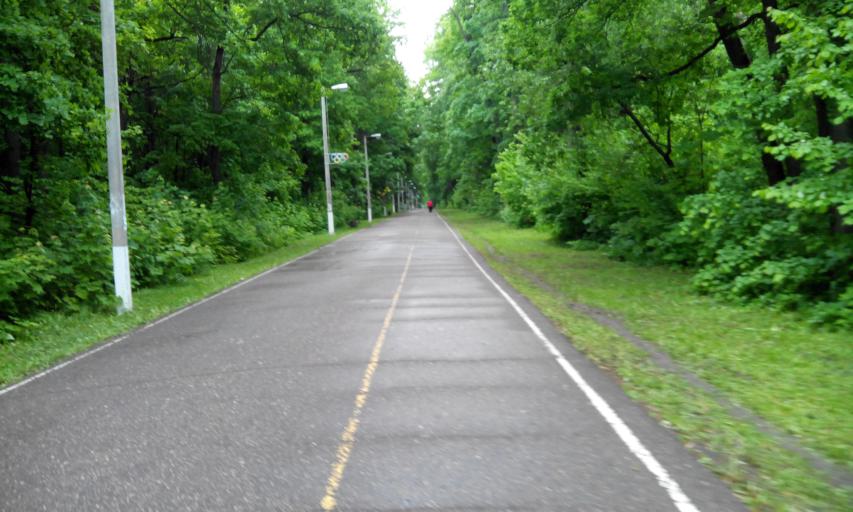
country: RU
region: Penza
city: Penza
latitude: 53.1813
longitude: 44.9750
